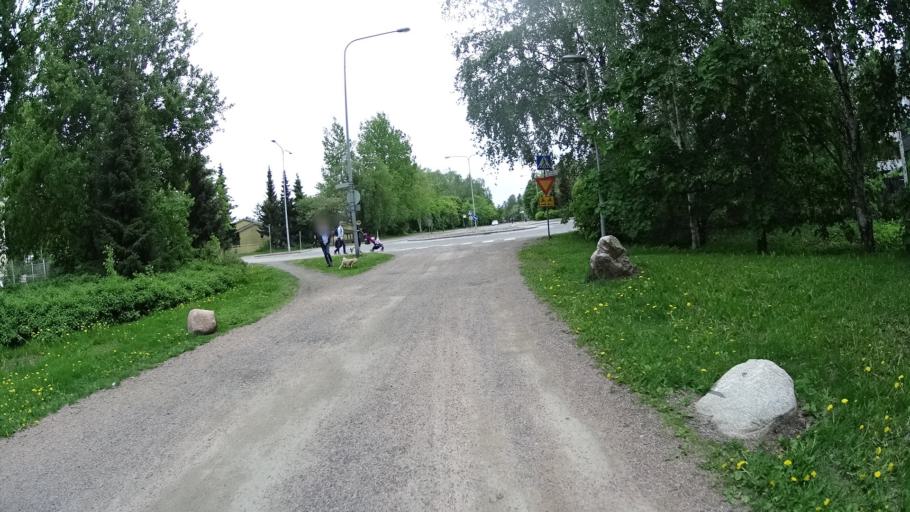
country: FI
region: Uusimaa
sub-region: Helsinki
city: Vantaa
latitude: 60.2704
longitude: 25.0623
